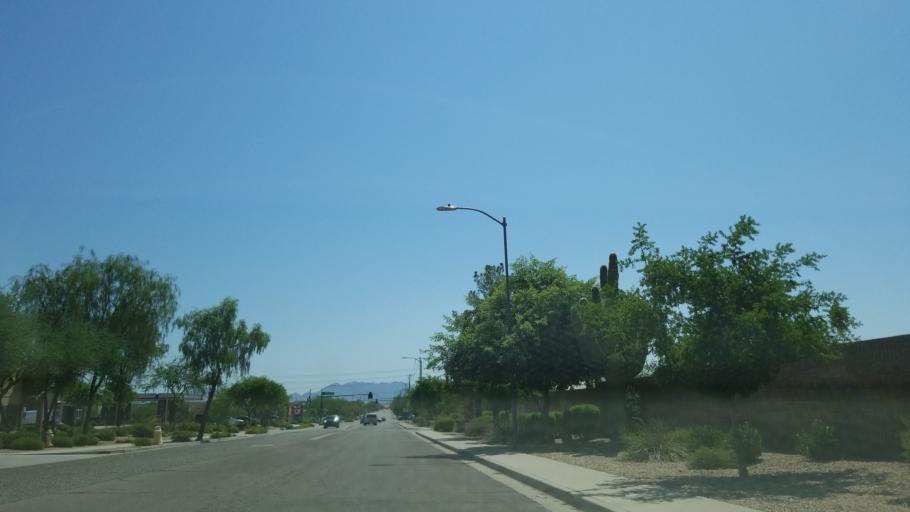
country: US
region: Arizona
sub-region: Maricopa County
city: Paradise Valley
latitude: 33.6768
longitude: -112.0333
